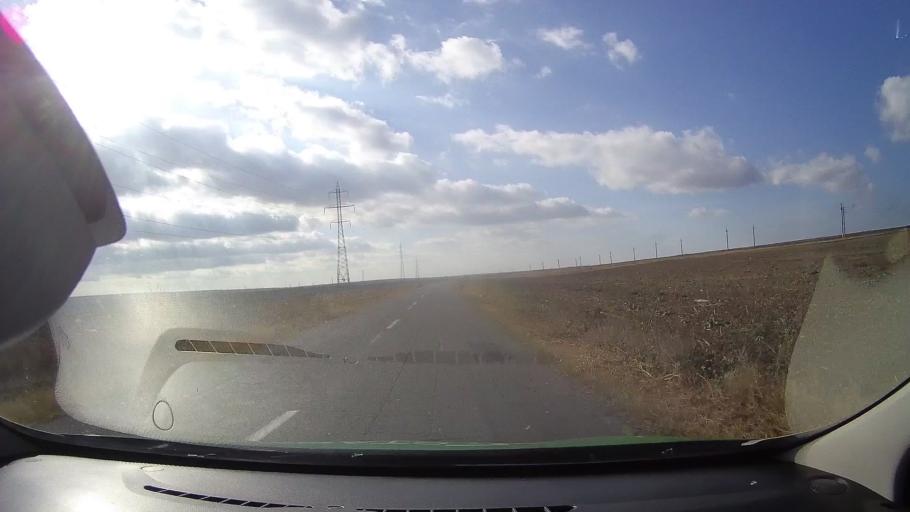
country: RO
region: Constanta
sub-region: Comuna Sacele
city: Sacele
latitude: 44.5061
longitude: 28.6692
